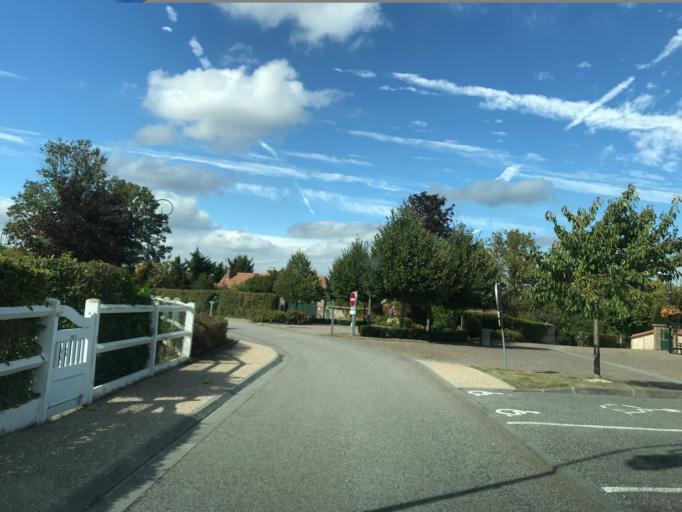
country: FR
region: Haute-Normandie
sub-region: Departement de l'Eure
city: Saint-Pierre-du-Vauvray
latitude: 49.2080
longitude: 1.2289
